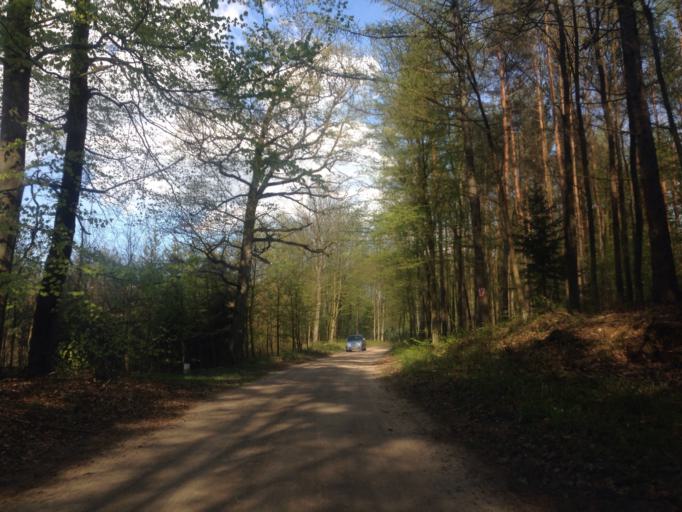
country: PL
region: Kujawsko-Pomorskie
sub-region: Powiat brodnicki
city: Gorzno
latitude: 53.2137
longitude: 19.7300
